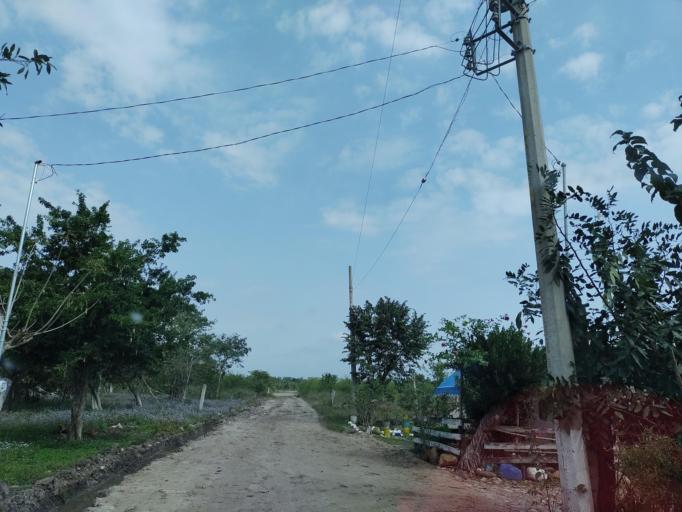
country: MX
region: Puebla
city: Espinal
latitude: 20.2804
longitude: -97.3354
